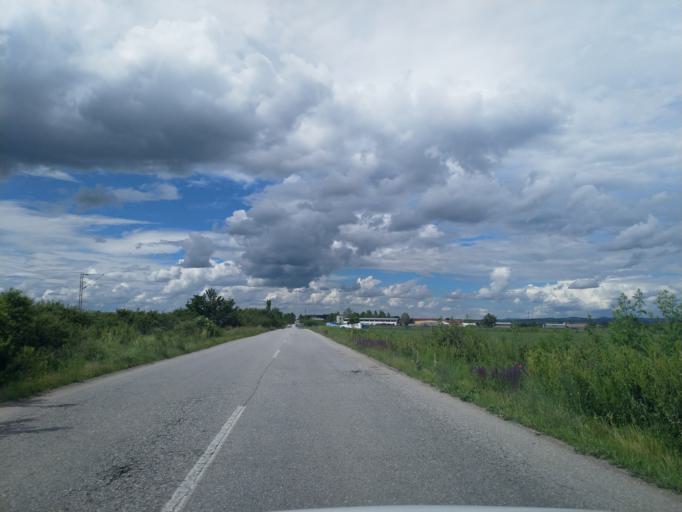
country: RS
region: Central Serbia
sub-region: Pomoravski Okrug
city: Cuprija
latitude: 43.8931
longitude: 21.3819
